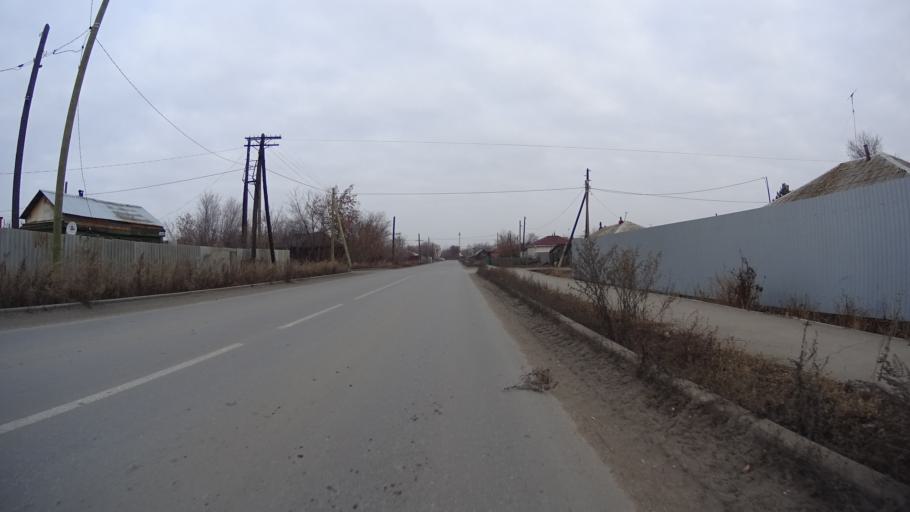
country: RU
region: Chelyabinsk
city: Troitsk
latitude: 54.1070
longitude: 61.5693
